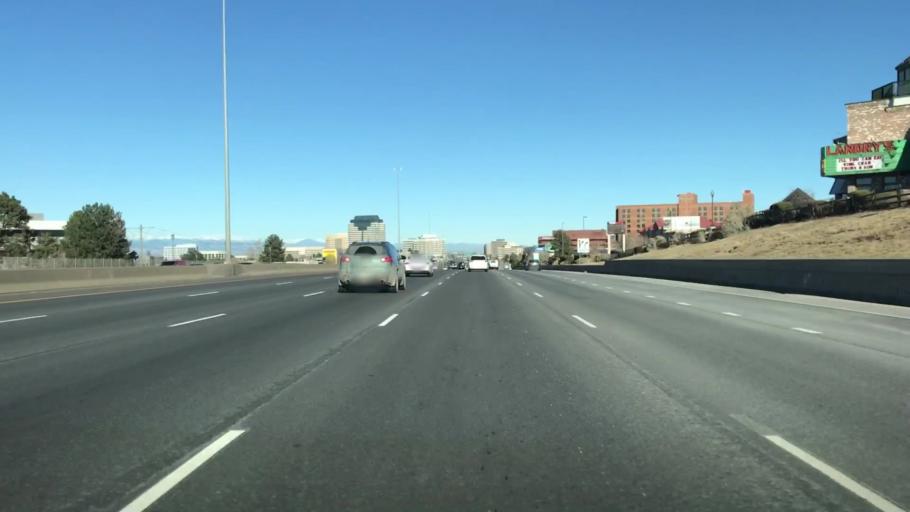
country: US
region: Colorado
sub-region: Arapahoe County
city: Centennial
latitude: 39.5856
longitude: -104.8794
